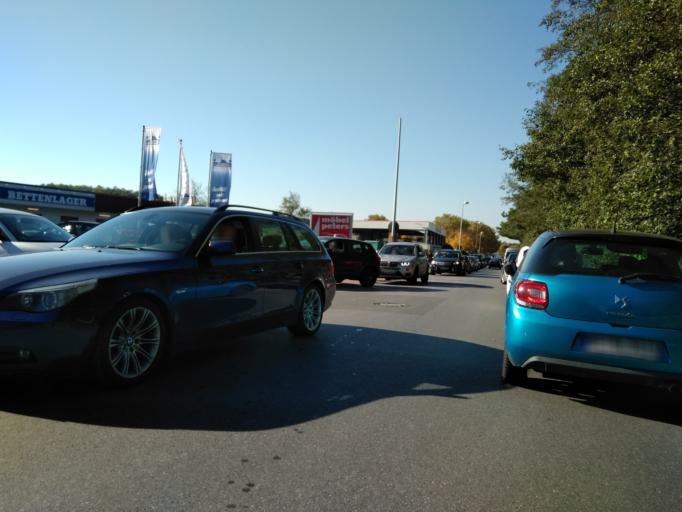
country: DE
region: North Rhine-Westphalia
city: Dorsten
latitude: 51.6592
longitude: 7.0162
